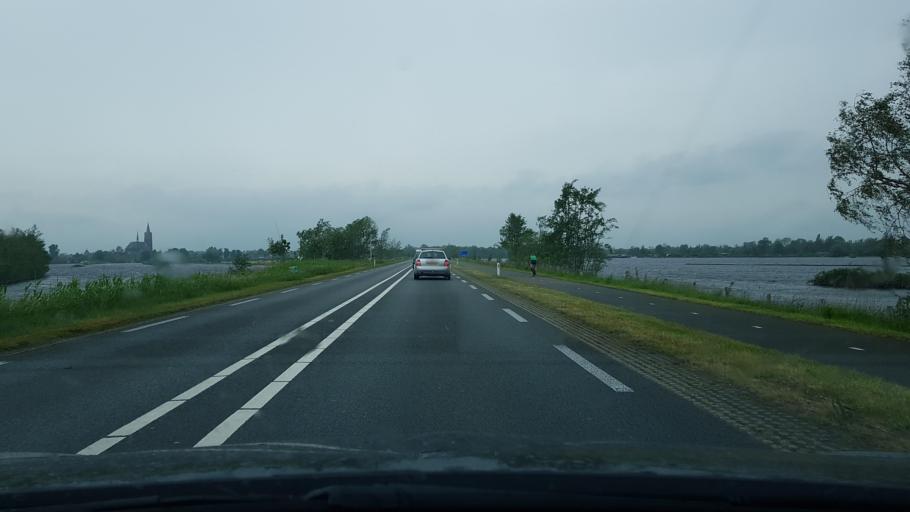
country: NL
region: Utrecht
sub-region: Stichtse Vecht
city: Breukelen
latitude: 52.2198
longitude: 4.9496
